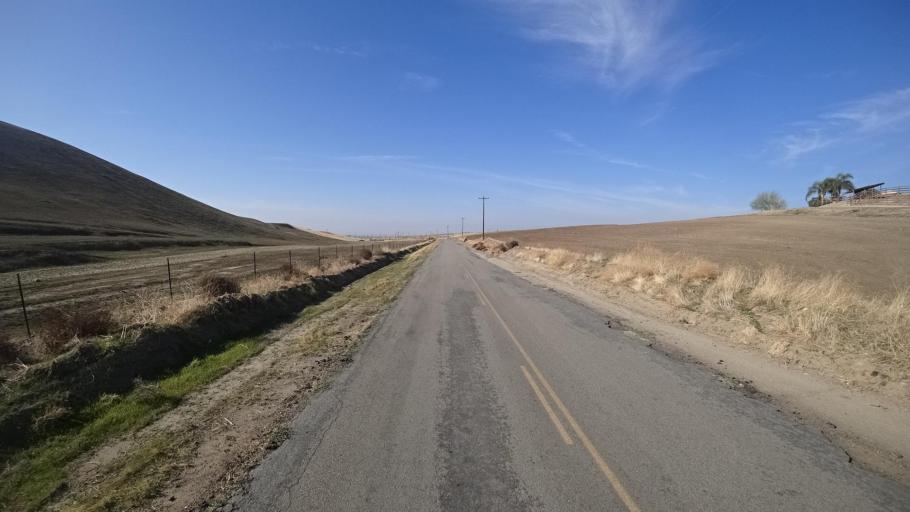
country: US
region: California
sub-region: Kern County
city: Lamont
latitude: 35.3798
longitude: -118.8314
